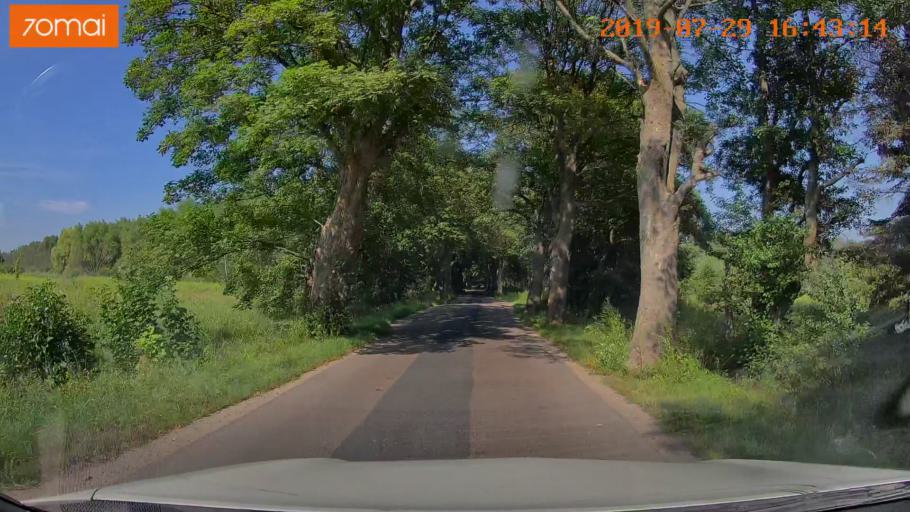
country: RU
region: Kaliningrad
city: Primorsk
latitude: 54.7477
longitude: 20.0820
